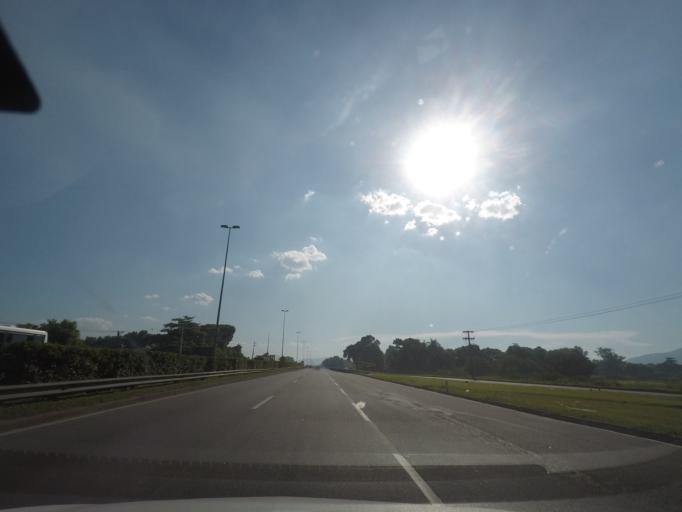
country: BR
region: Rio de Janeiro
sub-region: Duque De Caxias
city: Duque de Caxias
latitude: -22.6586
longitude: -43.2495
